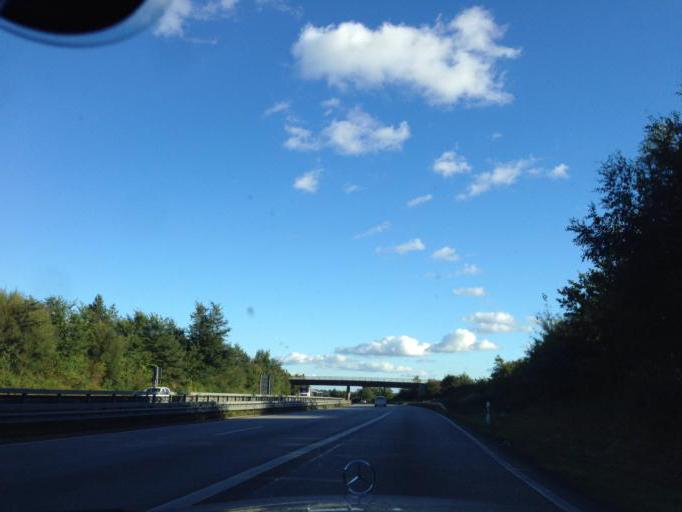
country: DE
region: Schleswig-Holstein
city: Schackendorf
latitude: 53.9586
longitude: 10.2626
